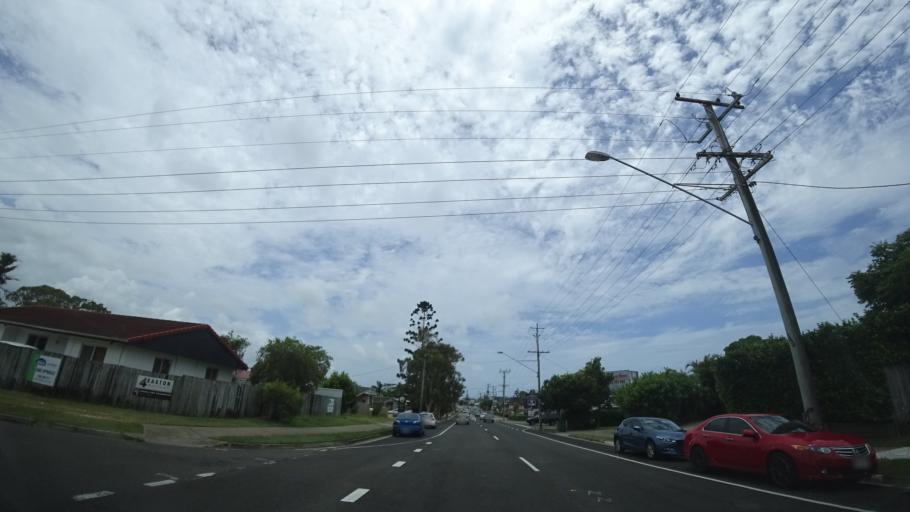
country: AU
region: Queensland
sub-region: Sunshine Coast
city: Mooloolaba
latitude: -26.6641
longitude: 153.0924
